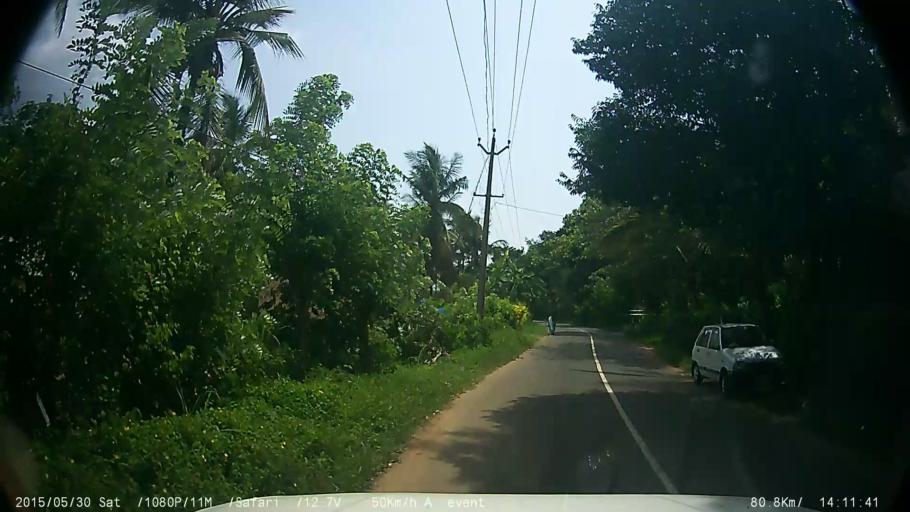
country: IN
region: Kerala
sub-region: Wayanad
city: Panamaram
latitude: 11.7906
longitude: 76.0527
